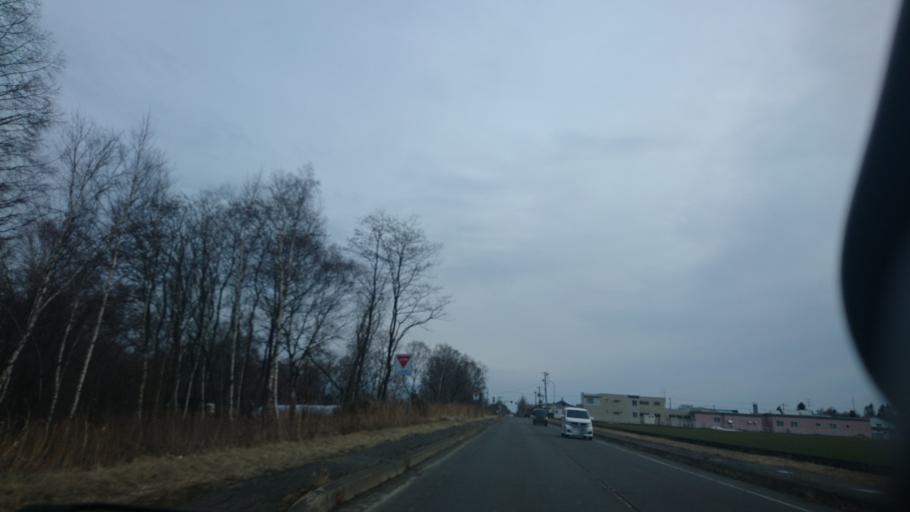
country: JP
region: Hokkaido
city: Otofuke
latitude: 42.9740
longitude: 143.1985
